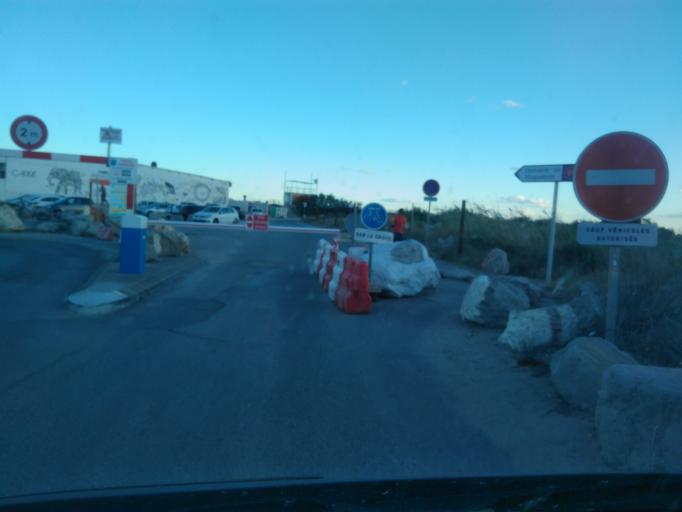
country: FR
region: Languedoc-Roussillon
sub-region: Departement de l'Herault
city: Palavas-les-Flots
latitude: 43.5174
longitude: 3.9049
